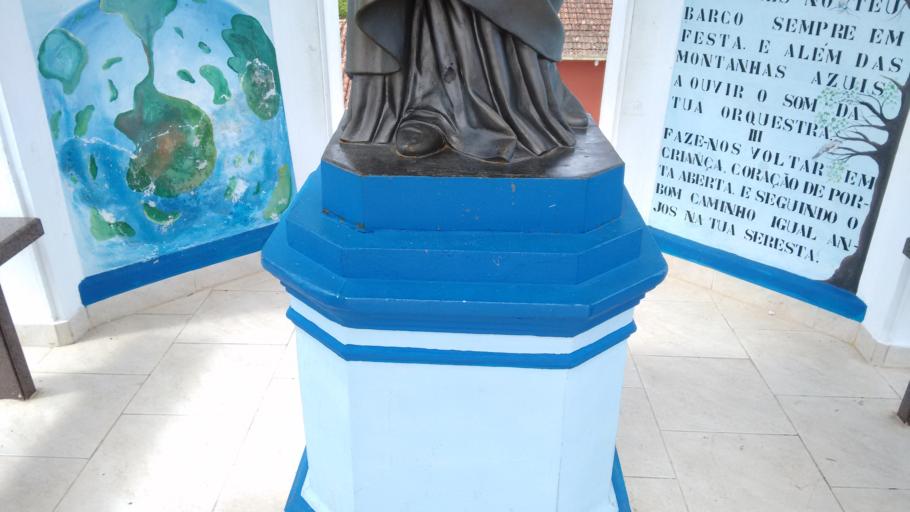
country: BR
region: Santa Catarina
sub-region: Sao Joao Batista
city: Sao Joao Batista
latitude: -27.2654
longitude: -48.9129
